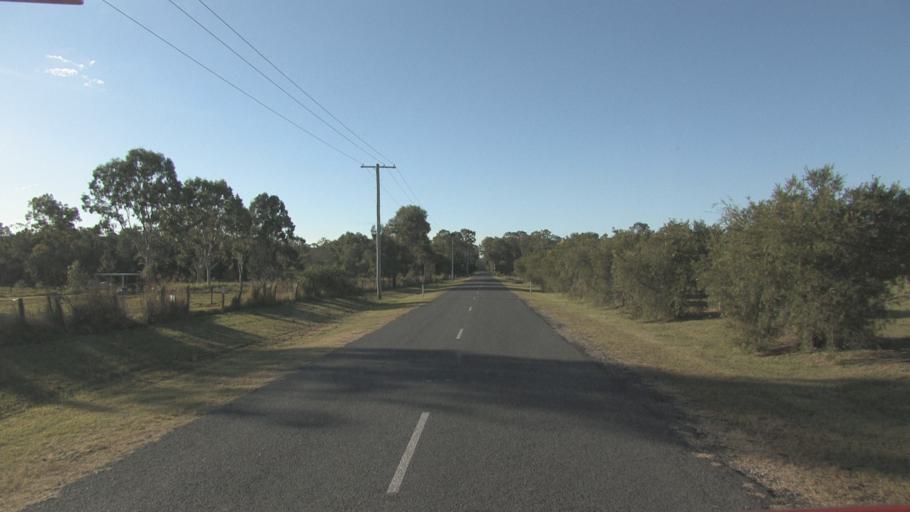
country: AU
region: Queensland
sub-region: Gold Coast
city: Yatala
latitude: -27.6773
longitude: 153.2429
